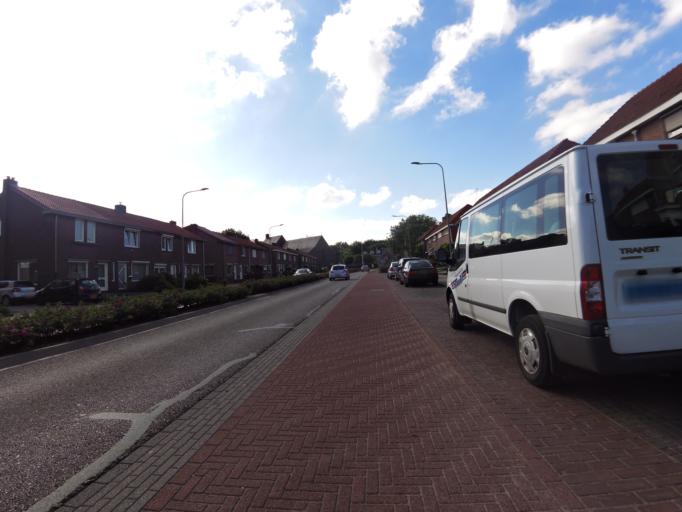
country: NL
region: Limburg
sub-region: Gemeente Brunssum
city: Brunssum
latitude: 50.9341
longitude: 5.9742
